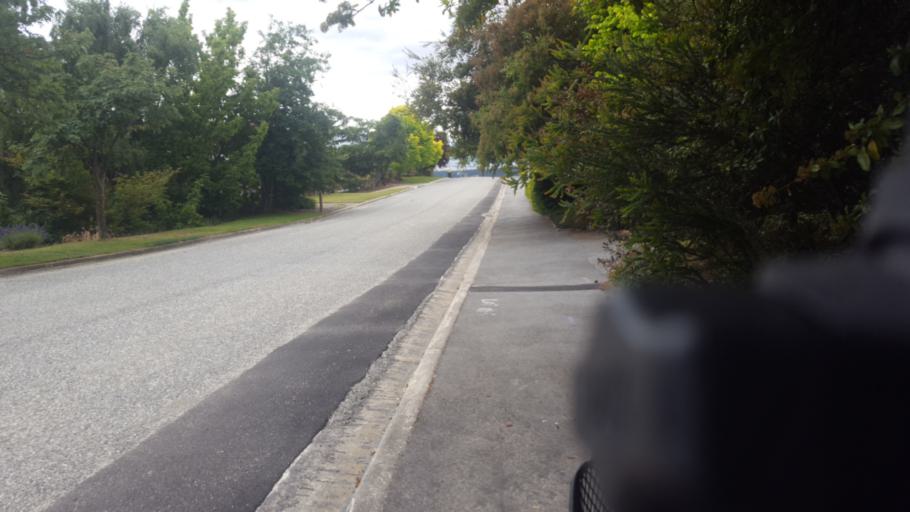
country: NZ
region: Otago
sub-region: Queenstown-Lakes District
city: Wanaka
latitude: -45.2619
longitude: 169.3773
